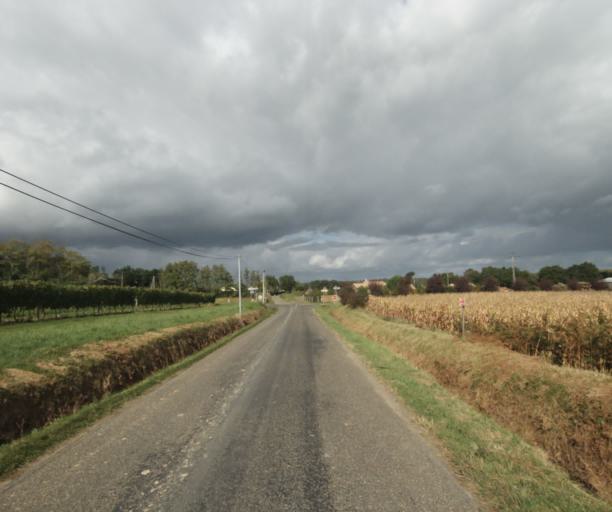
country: FR
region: Midi-Pyrenees
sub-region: Departement du Gers
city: Cazaubon
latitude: 43.8616
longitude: -0.0191
